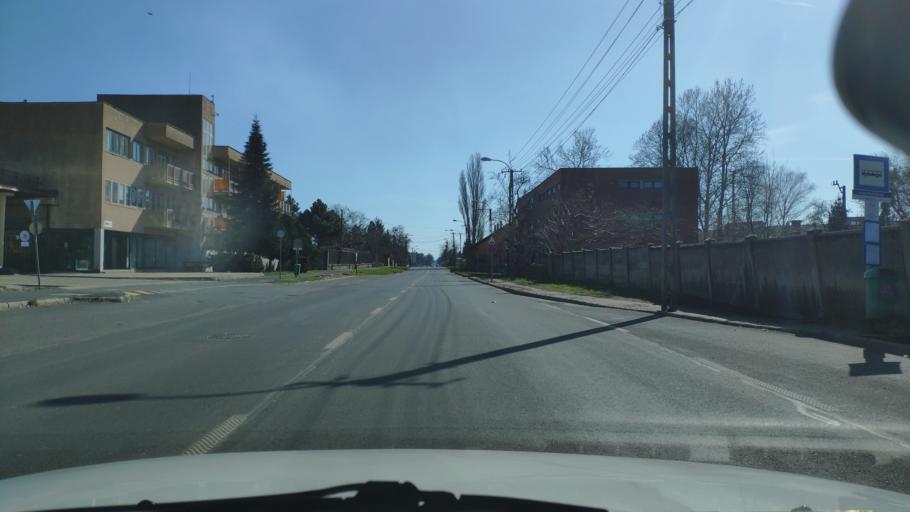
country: HU
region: Zala
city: Nagykanizsa
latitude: 46.4370
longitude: 16.9884
